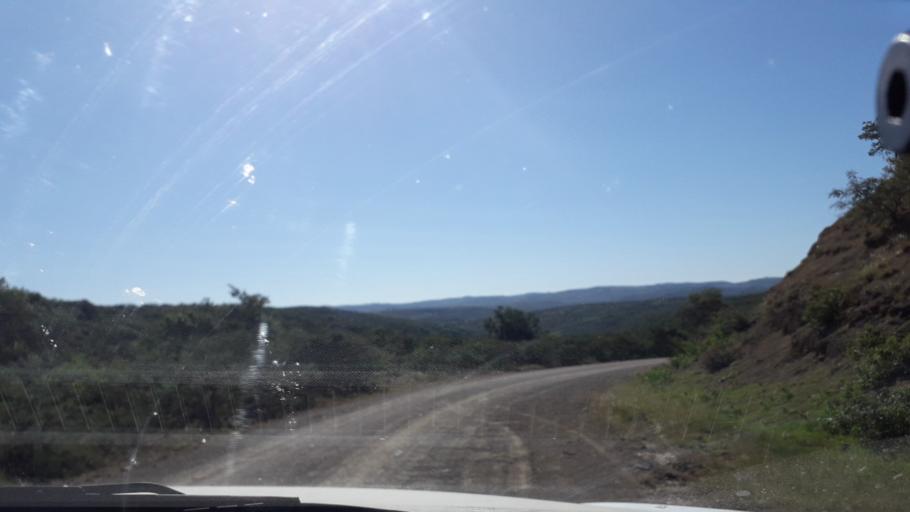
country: ZA
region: Eastern Cape
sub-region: Amathole District Municipality
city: Komga
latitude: -32.7782
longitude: 27.9581
